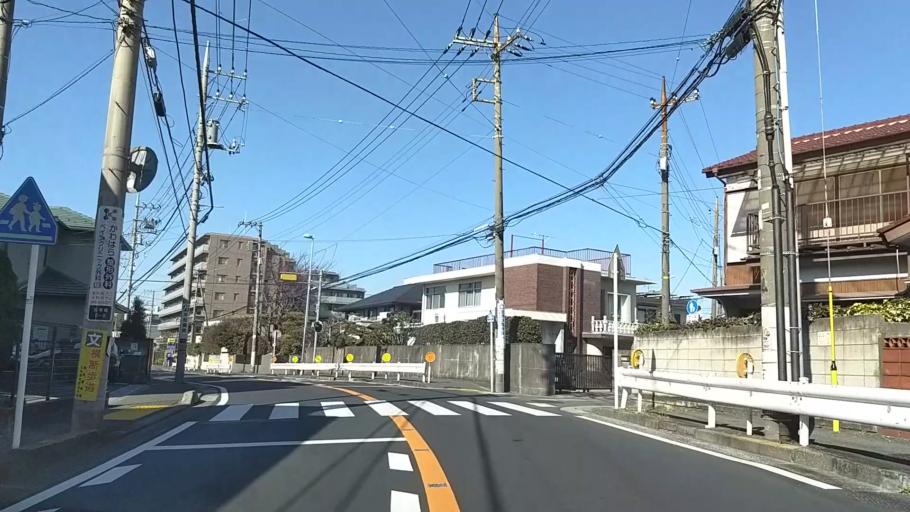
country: JP
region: Kanagawa
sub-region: Kawasaki-shi
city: Kawasaki
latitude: 35.5143
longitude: 139.6568
